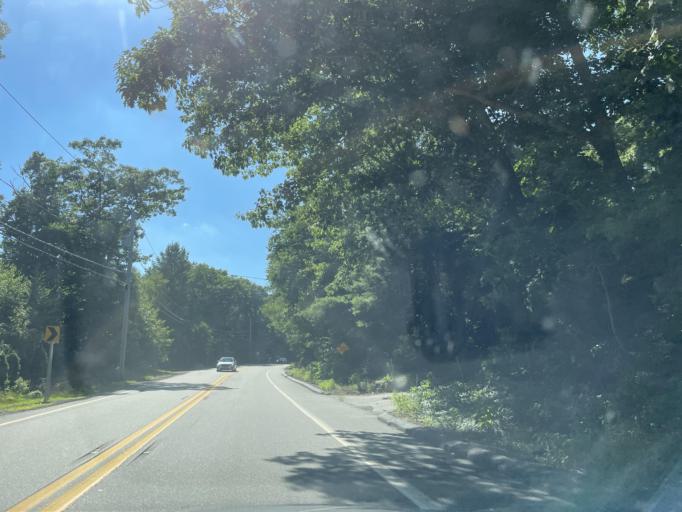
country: US
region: Massachusetts
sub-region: Worcester County
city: Douglas
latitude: 42.0534
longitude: -71.7516
